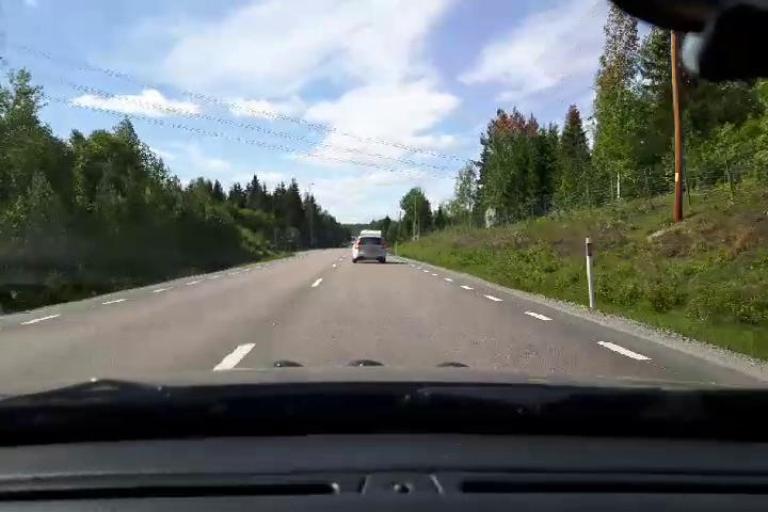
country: SE
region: Gaevleborg
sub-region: Bollnas Kommun
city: Kilafors
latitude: 61.2897
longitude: 16.5063
